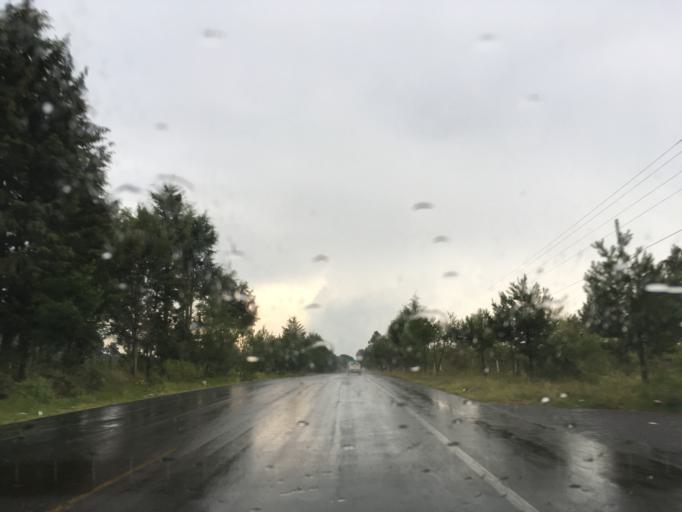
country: MX
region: Michoacan
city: Angahuan
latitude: 19.5253
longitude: -102.1870
